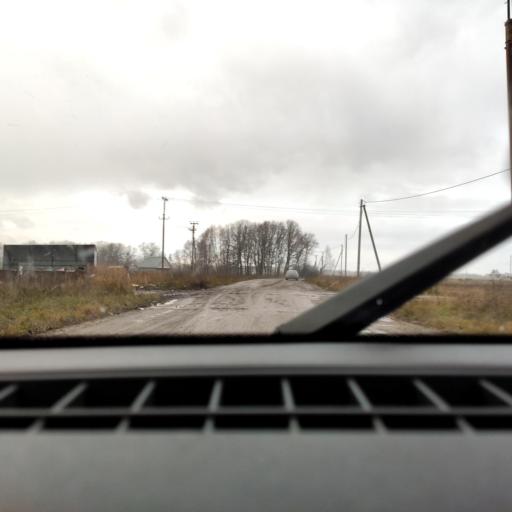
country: RU
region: Bashkortostan
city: Iglino
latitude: 54.7379
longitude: 56.3252
